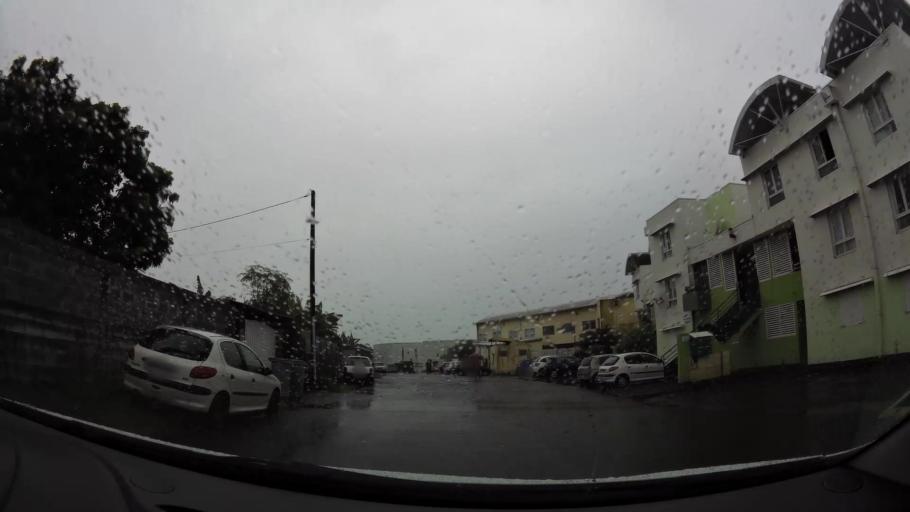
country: RE
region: Reunion
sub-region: Reunion
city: Saint-Andre
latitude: -20.9644
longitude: 55.6509
